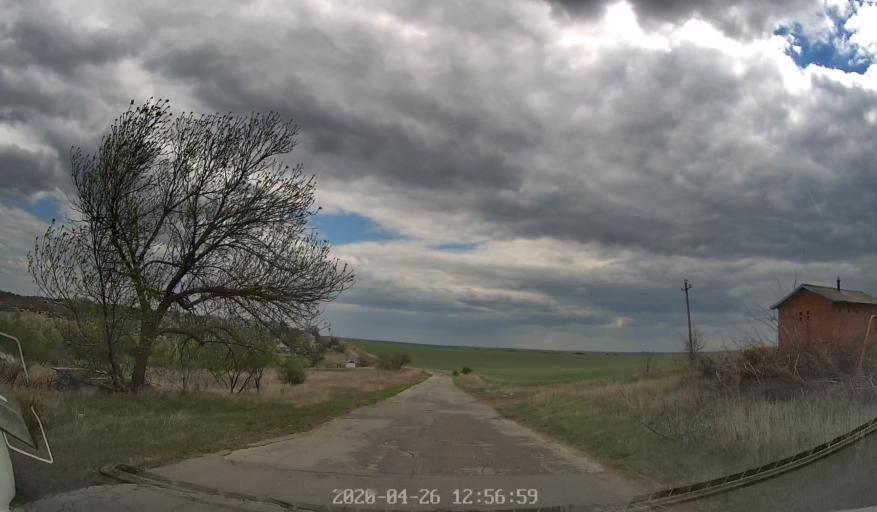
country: MD
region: Chisinau
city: Vadul lui Voda
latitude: 47.0696
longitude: 29.0691
